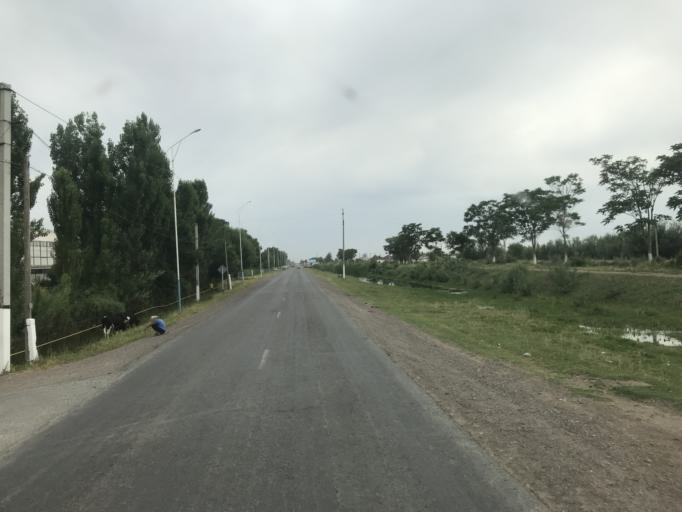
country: KZ
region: Ongtustik Qazaqstan
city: Asykata
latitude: 40.9379
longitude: 68.4122
